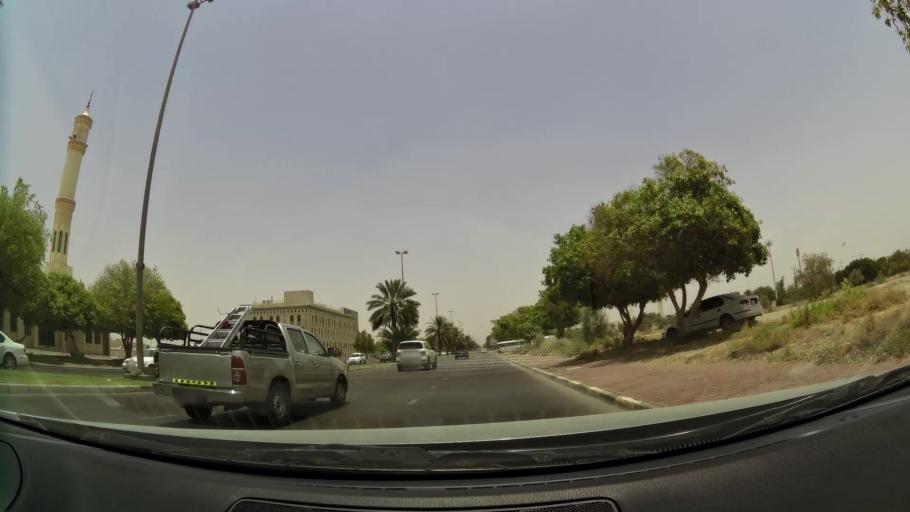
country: AE
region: Abu Dhabi
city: Al Ain
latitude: 24.2182
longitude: 55.7378
